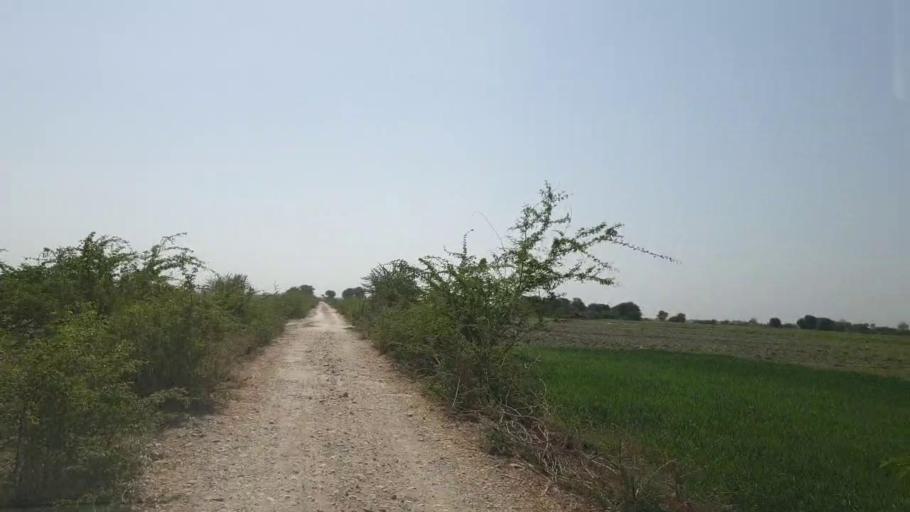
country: PK
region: Sindh
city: Naukot
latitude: 24.9110
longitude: 69.4877
